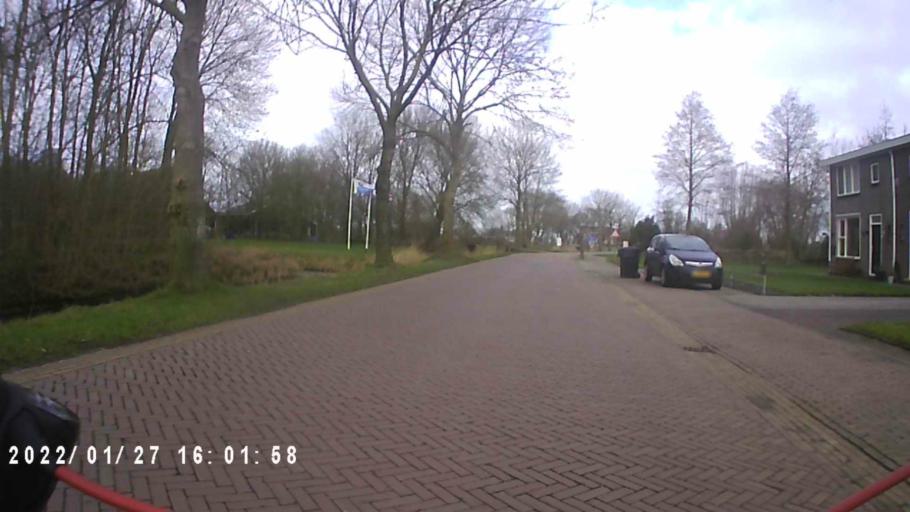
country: NL
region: Friesland
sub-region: Gemeente Dongeradeel
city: Anjum
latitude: 53.3741
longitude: 6.0886
